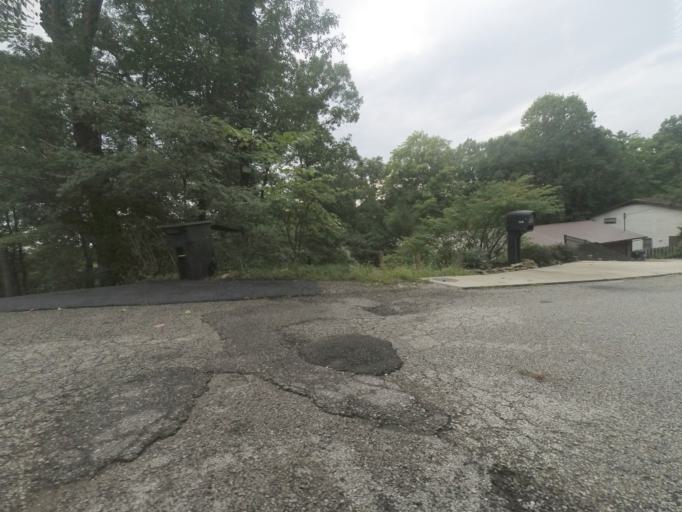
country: US
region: West Virginia
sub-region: Cabell County
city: Huntington
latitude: 38.3976
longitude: -82.4518
